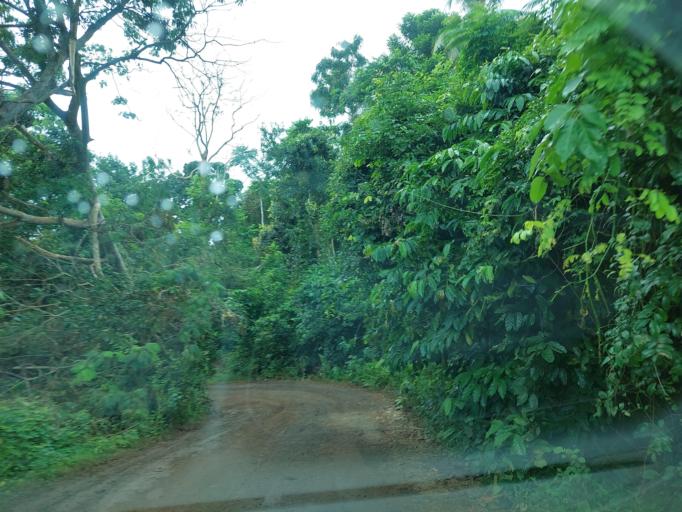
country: YT
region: Tsingoni
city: Tsingoni
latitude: -12.7634
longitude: 45.1233
